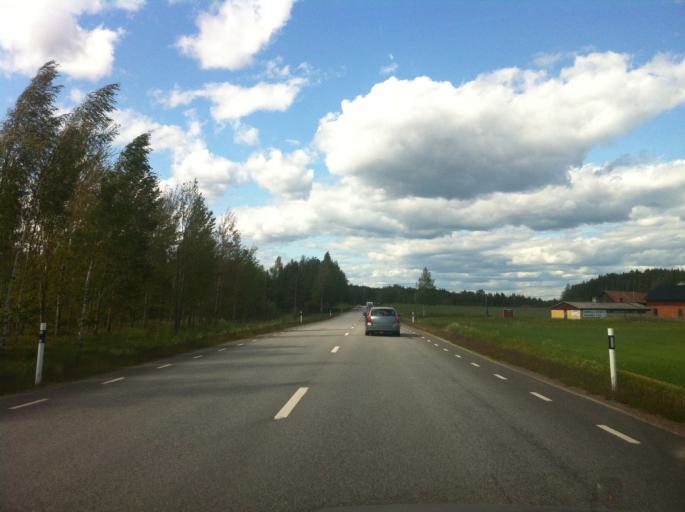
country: SE
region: Vaermland
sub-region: Storfors Kommun
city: Storfors
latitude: 59.4169
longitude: 14.2245
